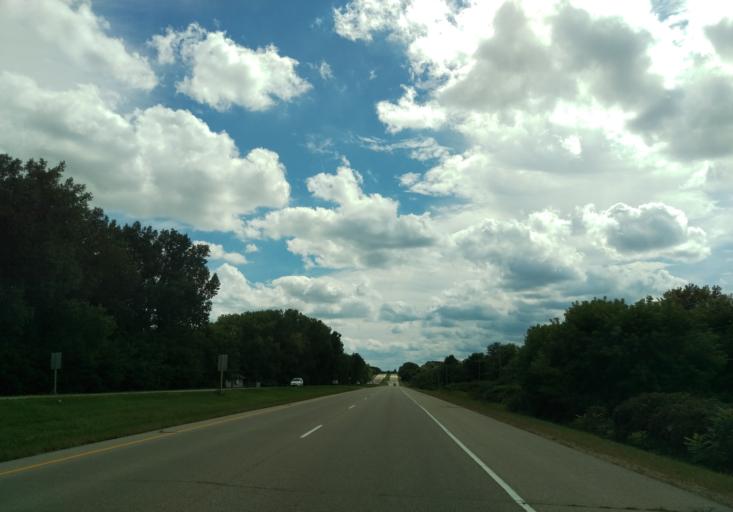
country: US
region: Wisconsin
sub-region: Dane County
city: Maple Bluff
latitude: 43.1500
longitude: -89.4012
